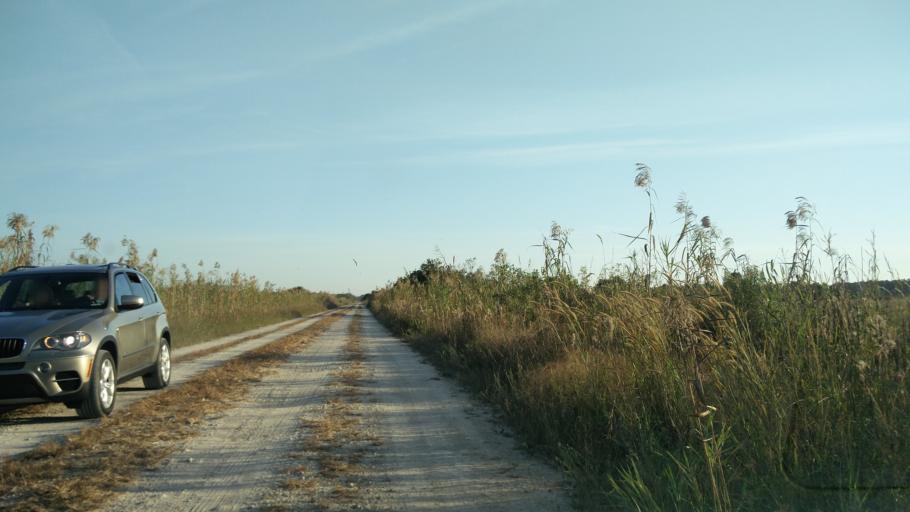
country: US
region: Florida
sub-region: Collier County
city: Lely Resort
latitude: 25.9677
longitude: -81.3666
